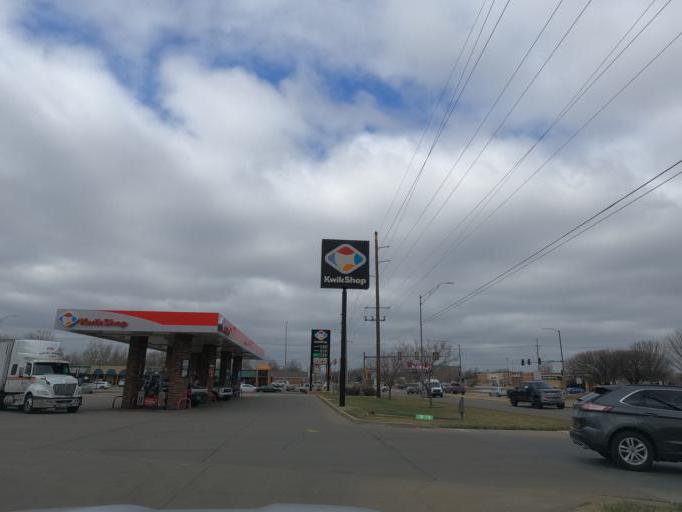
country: US
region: Kansas
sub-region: Reno County
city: Hutchinson
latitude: 38.0721
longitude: -97.9028
